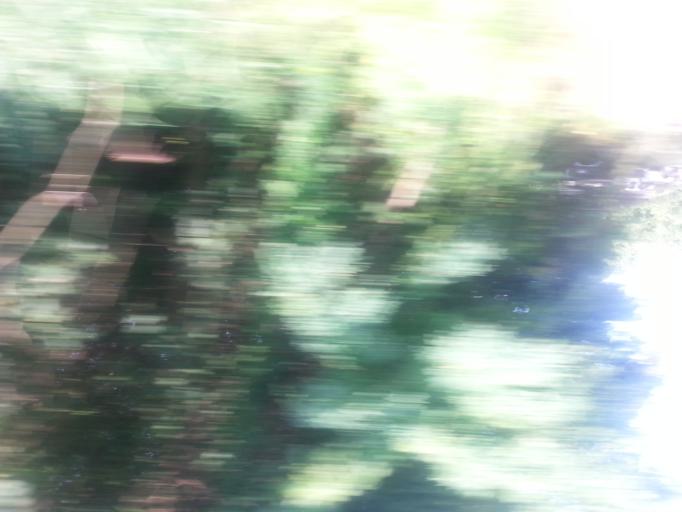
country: US
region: Tennessee
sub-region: Sevier County
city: Seymour
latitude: 35.8547
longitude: -83.7767
